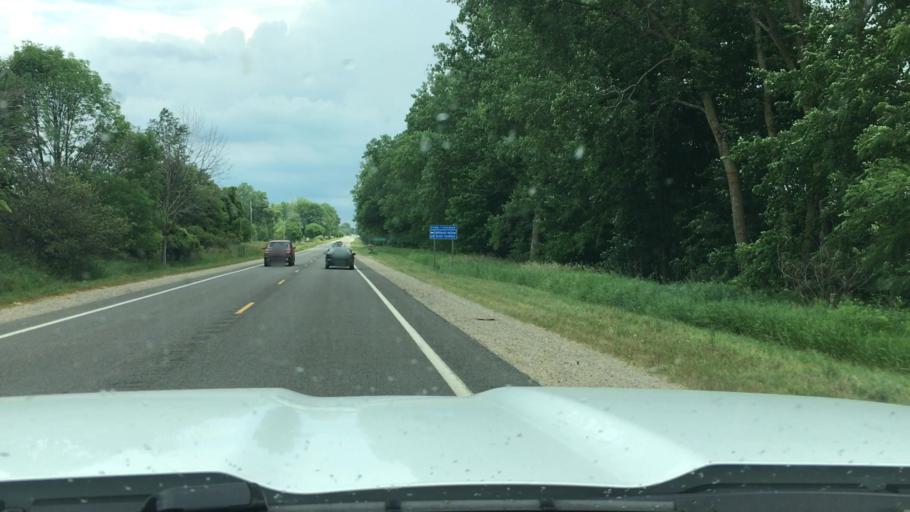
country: US
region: Michigan
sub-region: Montcalm County
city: Stanton
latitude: 43.1775
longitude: -85.0192
